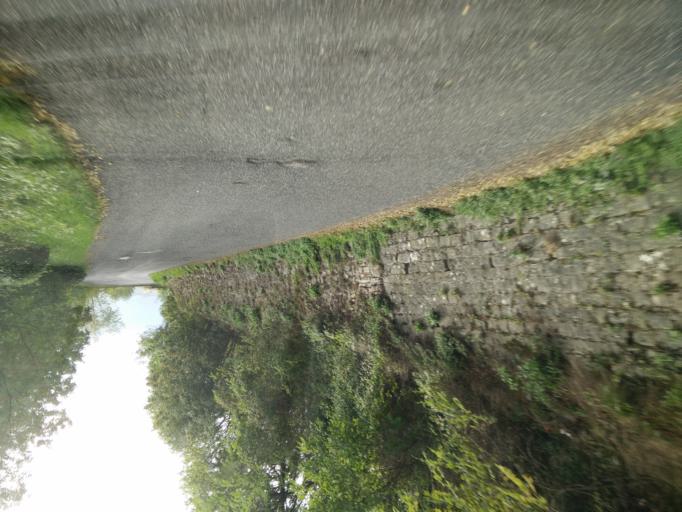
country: IT
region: Tuscany
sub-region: Provincia di Massa-Carrara
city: Pontremoli
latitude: 44.3699
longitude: 9.8305
